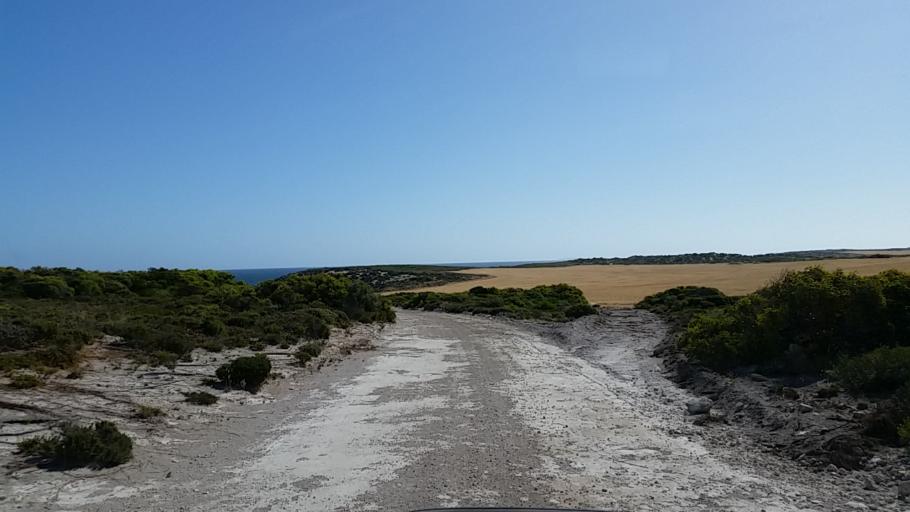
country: AU
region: South Australia
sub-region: Yorke Peninsula
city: Honiton
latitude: -35.2376
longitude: 137.1489
